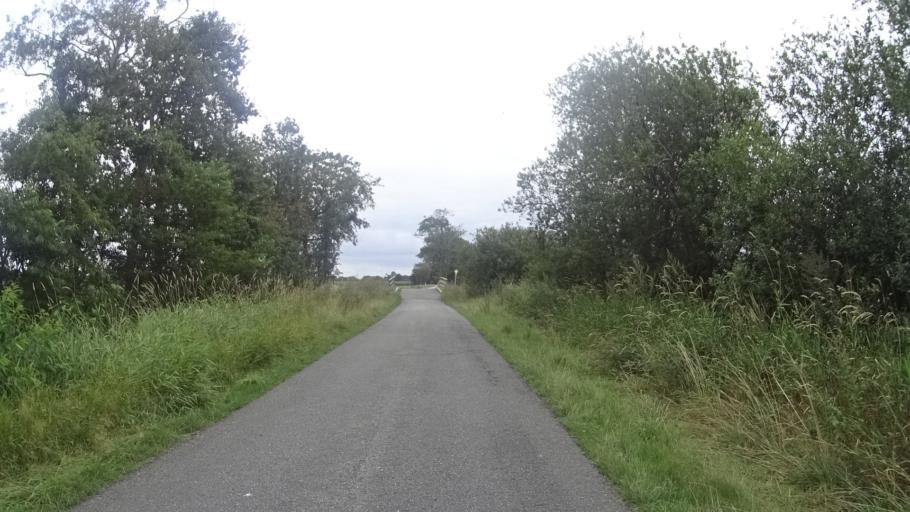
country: DE
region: Lower Saxony
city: Odisheim
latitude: 53.6382
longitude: 8.9245
